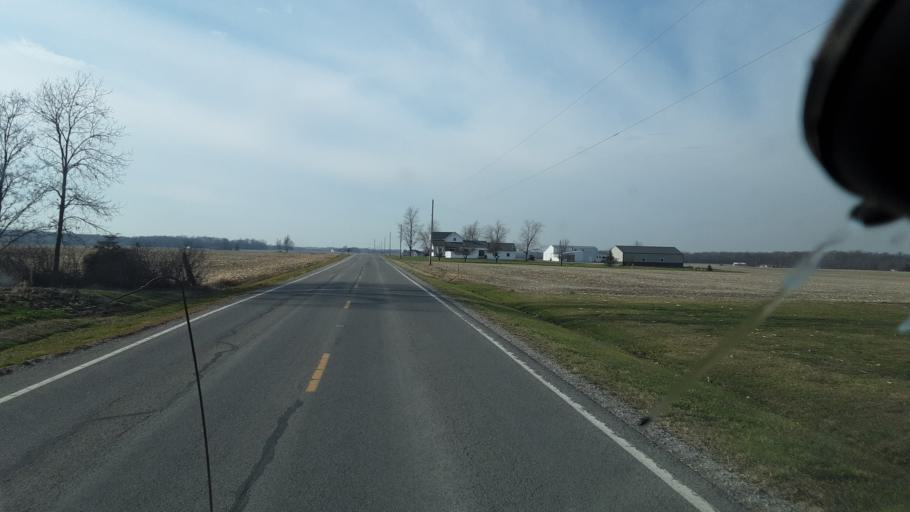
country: US
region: Ohio
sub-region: Williams County
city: Edgerton
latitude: 41.3827
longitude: -84.7571
